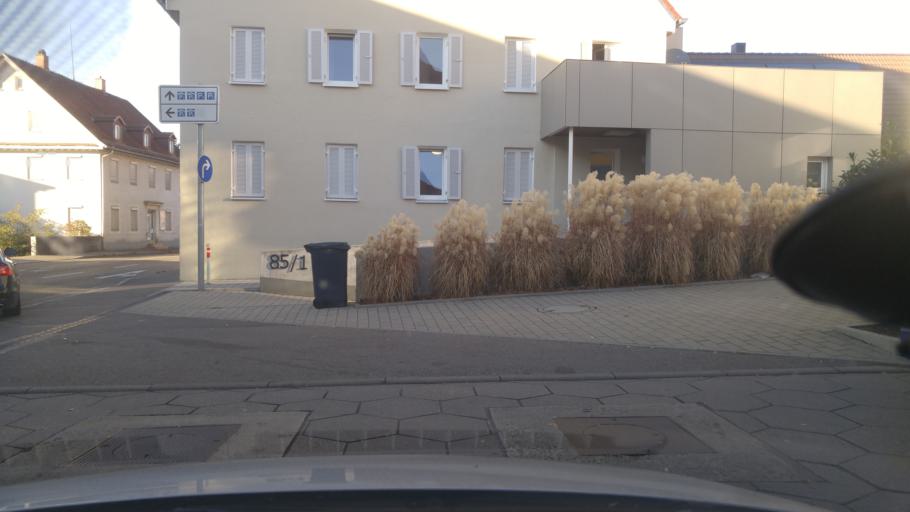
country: DE
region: Baden-Wuerttemberg
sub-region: Regierungsbezirk Stuttgart
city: Kirchheim unter Teck
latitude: 48.6409
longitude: 9.4533
